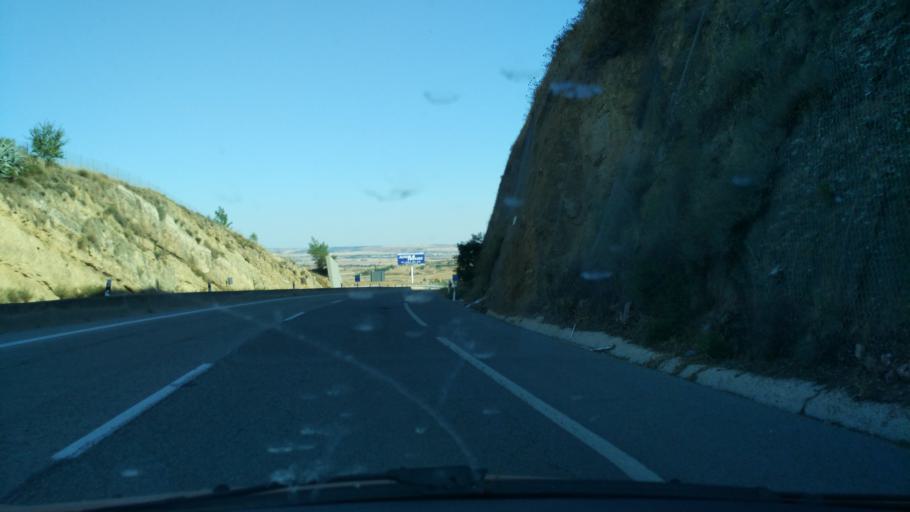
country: ES
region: Madrid
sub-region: Provincia de Madrid
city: El Molar
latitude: 40.7293
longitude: -3.5806
